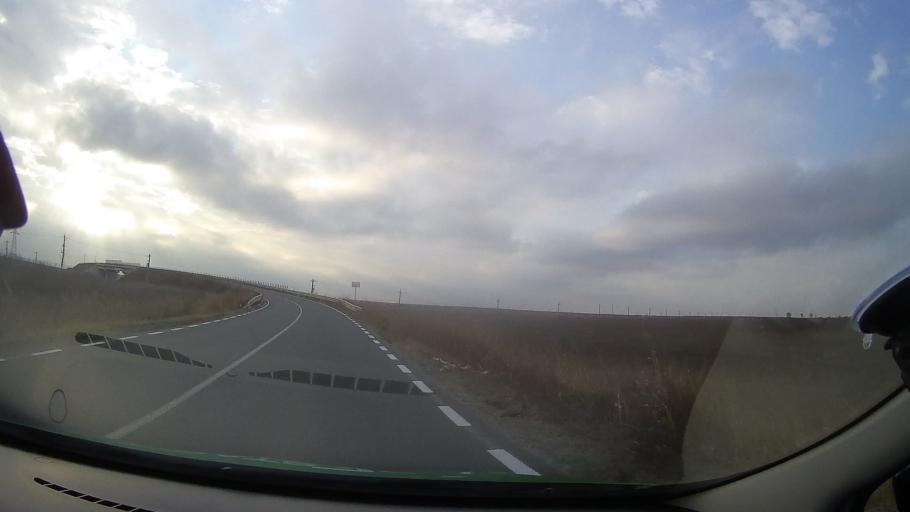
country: RO
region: Constanta
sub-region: Comuna Mircea Voda
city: Satu Nou
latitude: 44.2209
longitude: 28.1979
